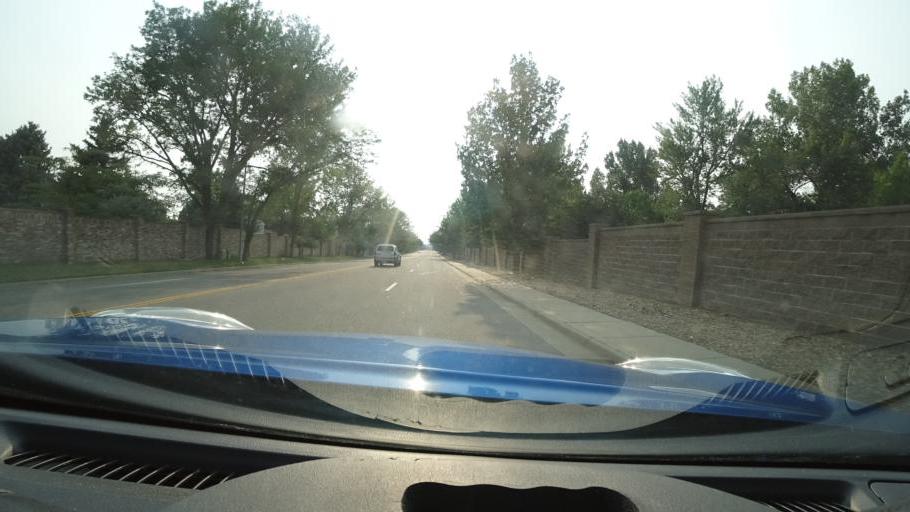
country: US
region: Colorado
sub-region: Adams County
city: Aurora
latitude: 39.6676
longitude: -104.8545
